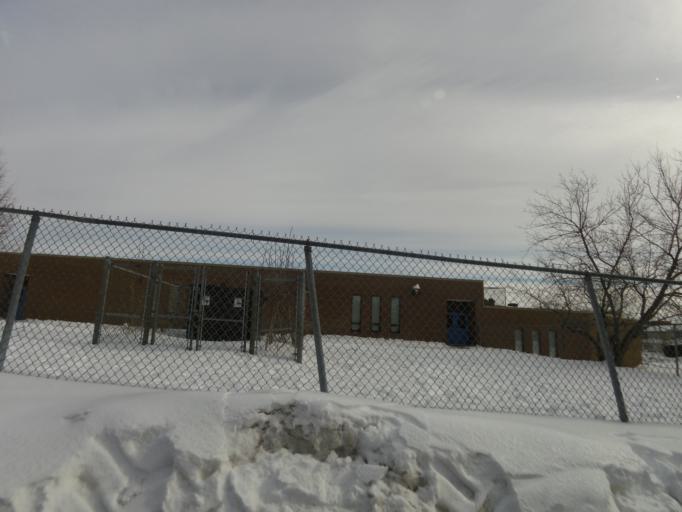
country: CA
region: Ontario
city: Ottawa
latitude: 45.4437
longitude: -75.6001
